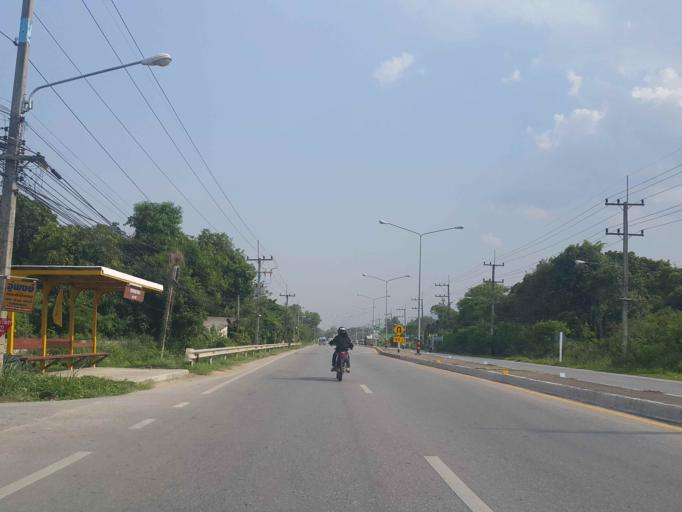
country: TH
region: Chiang Mai
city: Mae Taeng
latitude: 19.0114
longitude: 98.9446
